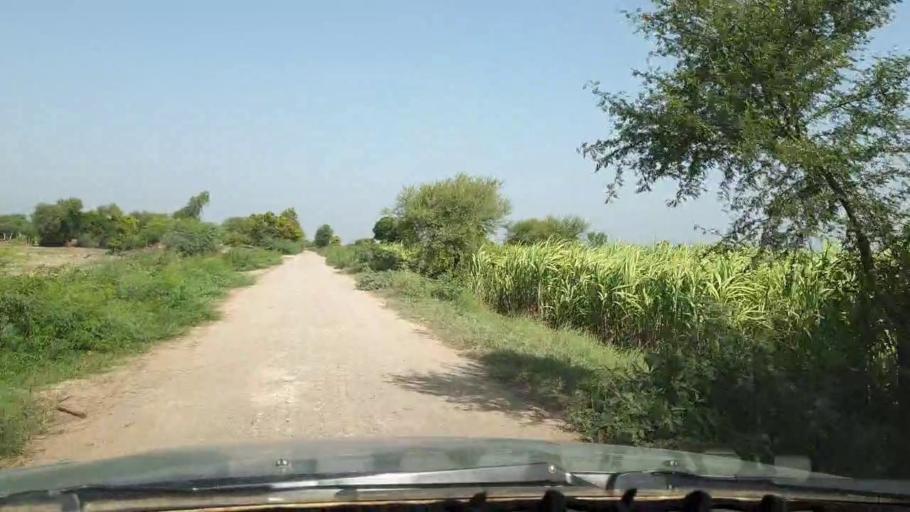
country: PK
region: Sindh
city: Matli
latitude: 25.0902
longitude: 68.6112
